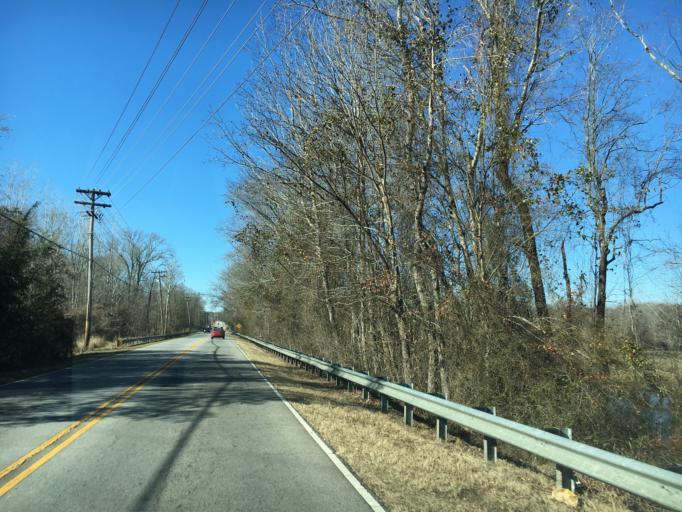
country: US
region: South Carolina
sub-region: Anderson County
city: Anderson
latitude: 34.5044
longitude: -82.6180
